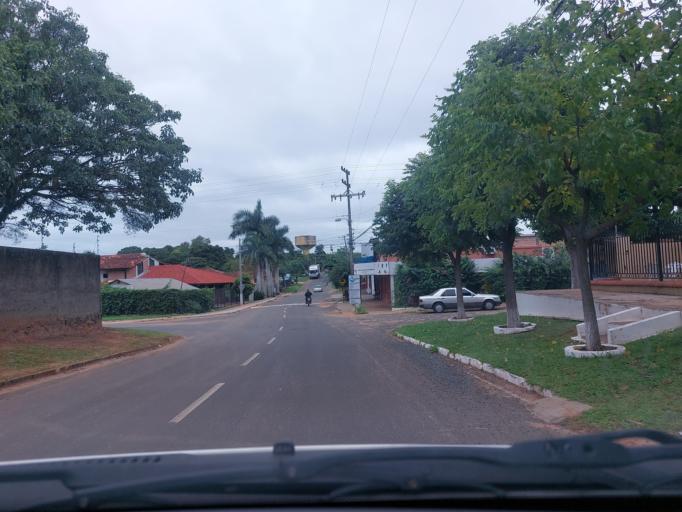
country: PY
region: San Pedro
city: Guayaybi
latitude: -24.6728
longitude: -56.4446
